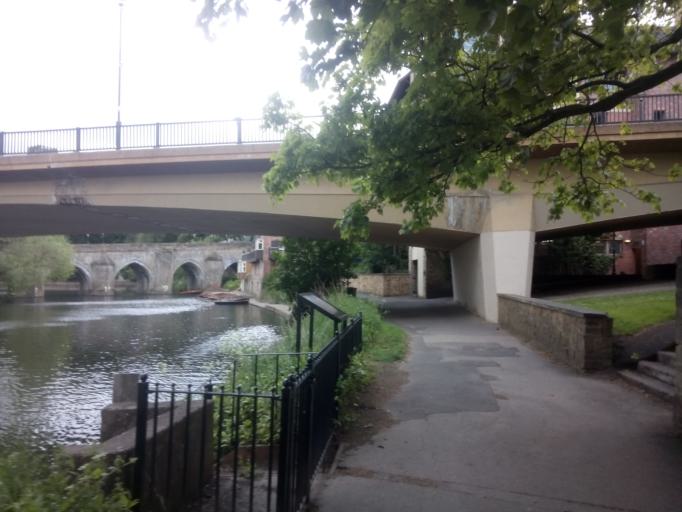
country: GB
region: England
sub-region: County Durham
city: Durham
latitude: 54.7767
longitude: -1.5720
